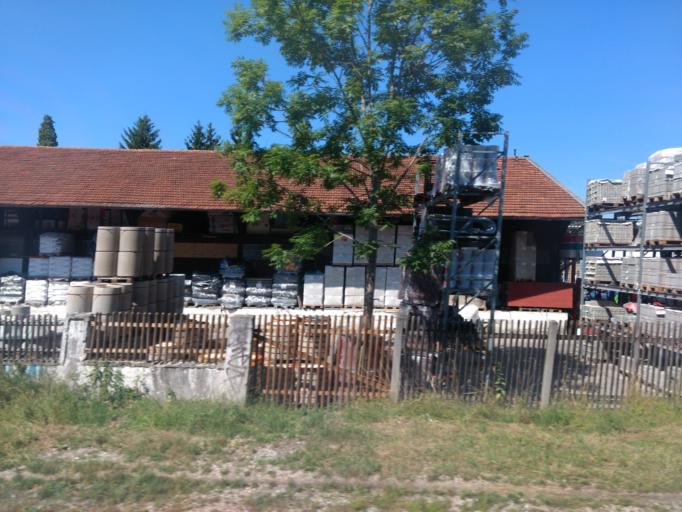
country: DE
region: Bavaria
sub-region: Upper Bavaria
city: Bogenhausen
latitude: 48.1548
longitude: 11.6489
